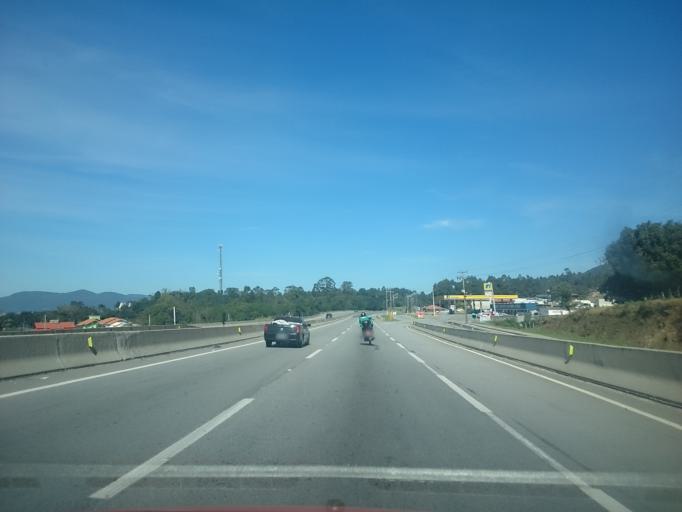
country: BR
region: Santa Catarina
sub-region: Palhoca
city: Palhoca
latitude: -27.7201
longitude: -48.6460
